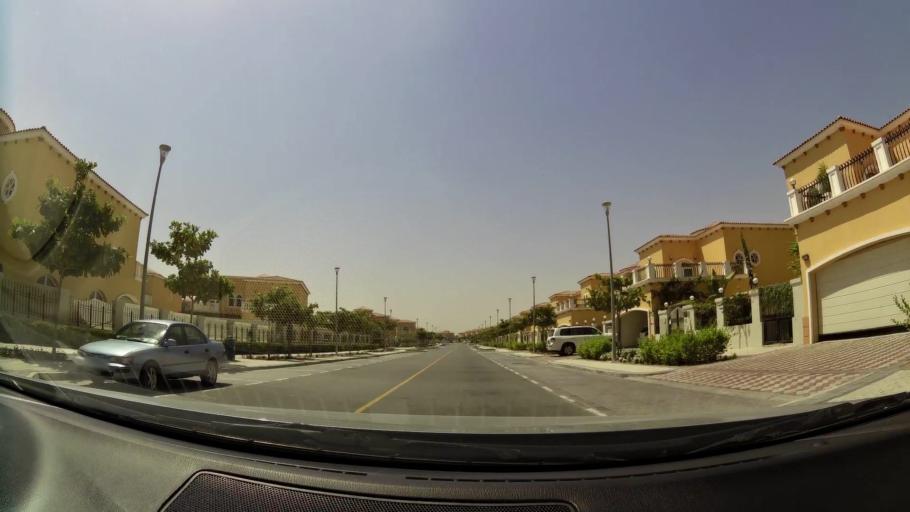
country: AE
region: Dubai
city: Dubai
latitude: 25.0588
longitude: 55.1426
